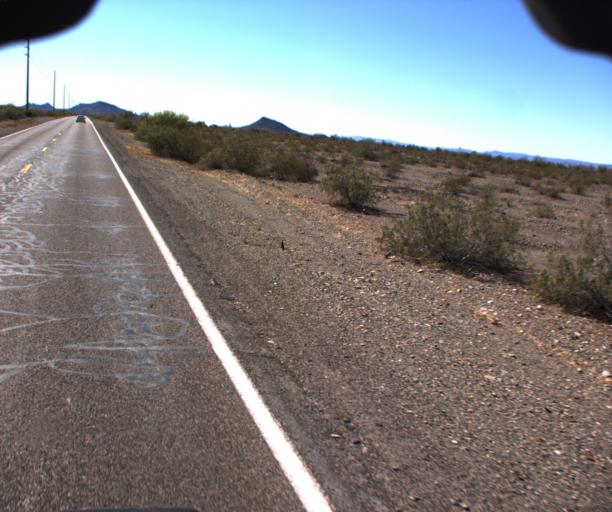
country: US
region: Arizona
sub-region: La Paz County
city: Salome
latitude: 33.7590
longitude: -113.7799
